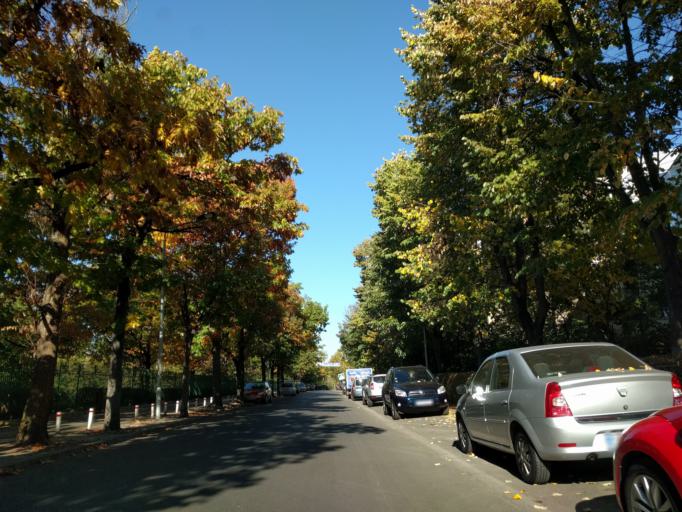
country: RO
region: Ilfov
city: Dobroesti
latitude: 44.4226
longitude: 26.1586
